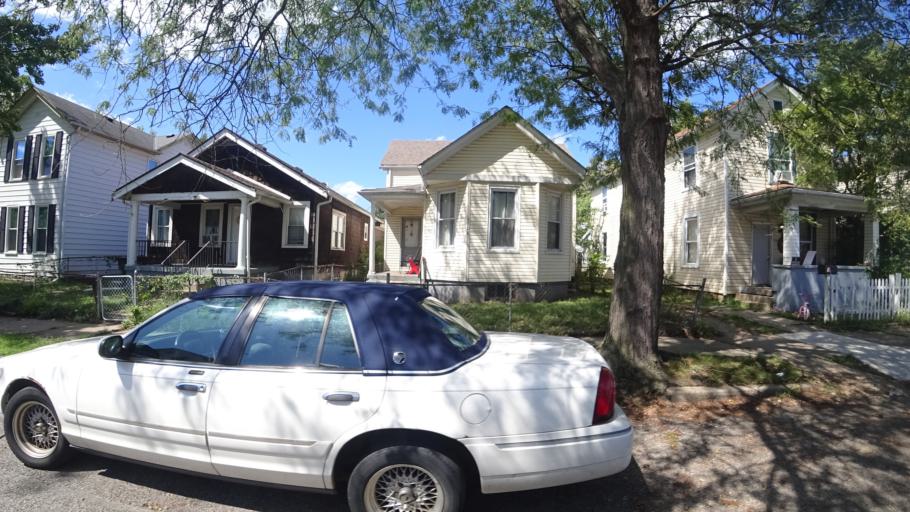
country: US
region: Ohio
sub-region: Butler County
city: Hamilton
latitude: 39.4051
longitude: -84.5464
